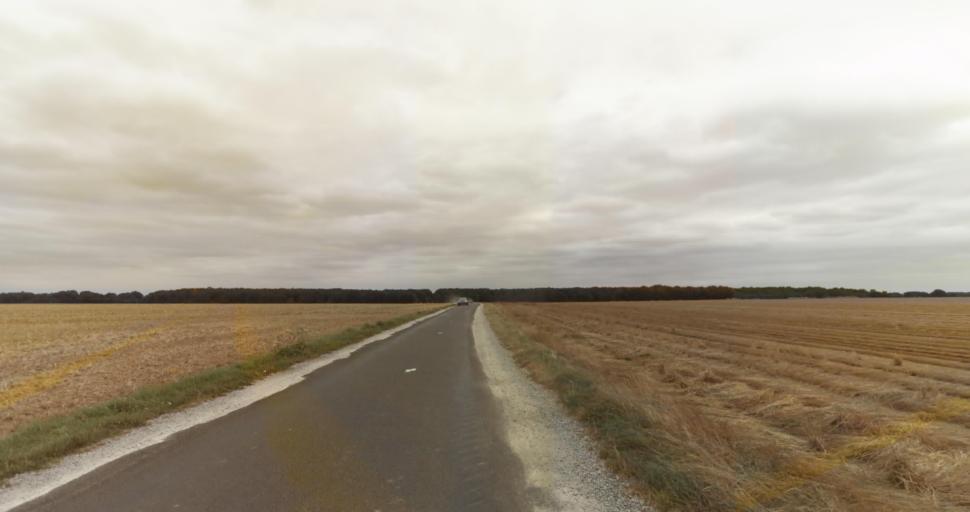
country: FR
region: Haute-Normandie
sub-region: Departement de l'Eure
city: Evreux
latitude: 48.9617
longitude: 1.2360
